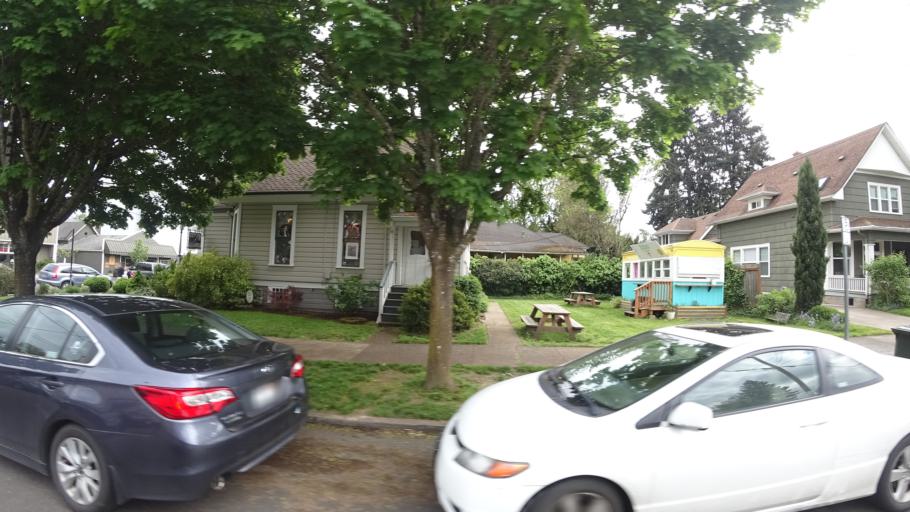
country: US
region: Oregon
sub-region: Clackamas County
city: Milwaukie
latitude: 45.4657
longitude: -122.6534
